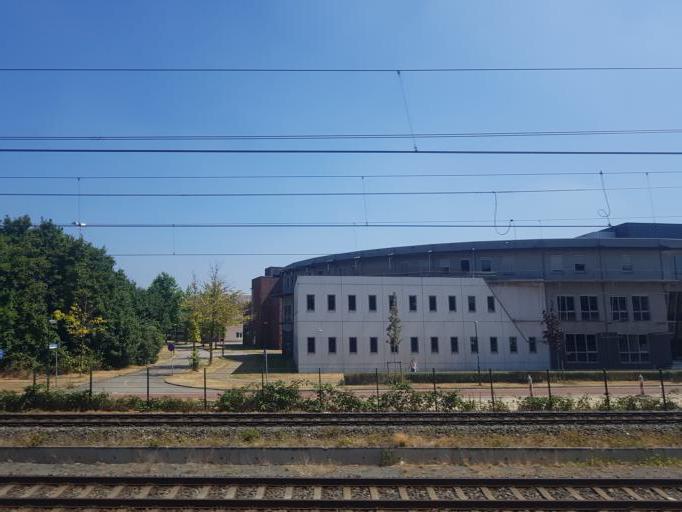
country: NL
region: Utrecht
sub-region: Gemeente Houten
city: Houten
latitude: 52.0262
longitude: 5.1734
